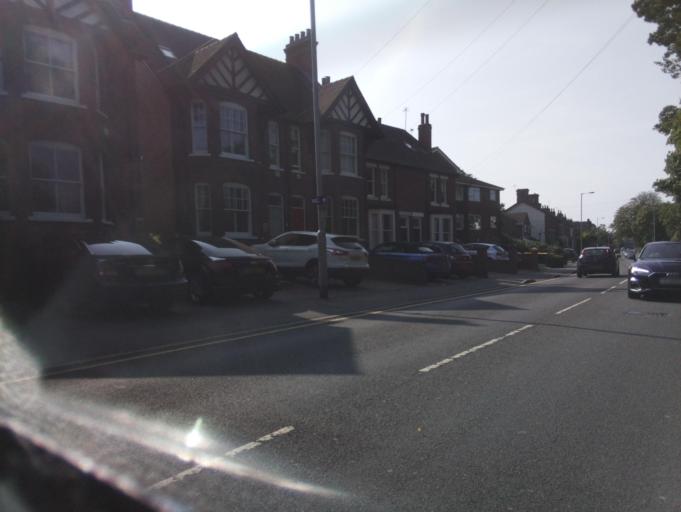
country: GB
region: England
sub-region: Staffordshire
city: Lichfield
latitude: 52.6789
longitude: -1.8286
